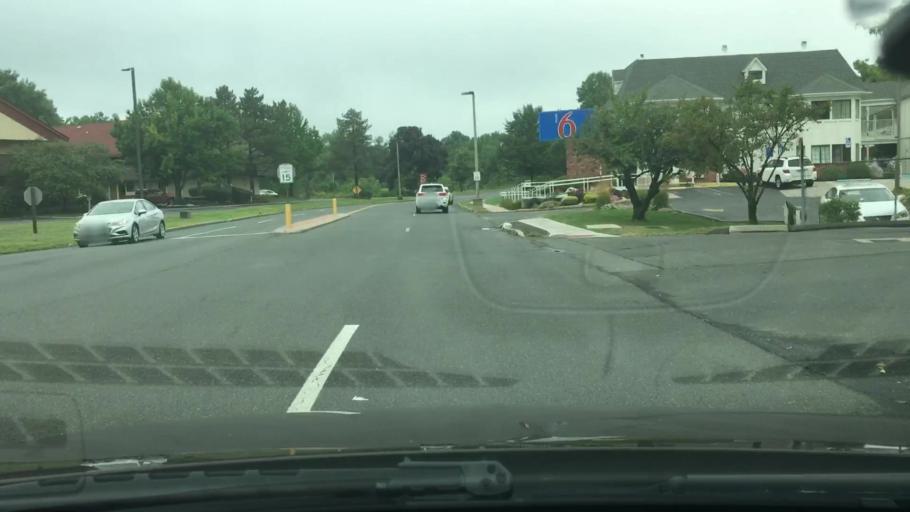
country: US
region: Connecticut
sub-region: Hartford County
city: Enfield
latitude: 41.9907
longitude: -72.5837
